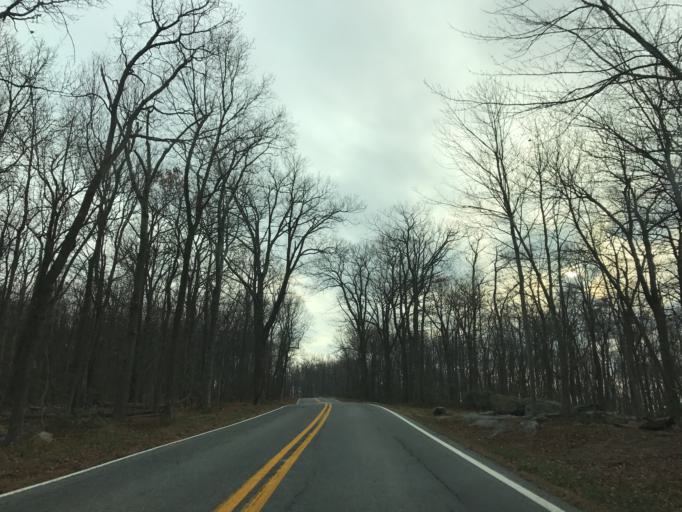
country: US
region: Maryland
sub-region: Frederick County
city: Myersville
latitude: 39.4970
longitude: -77.4997
